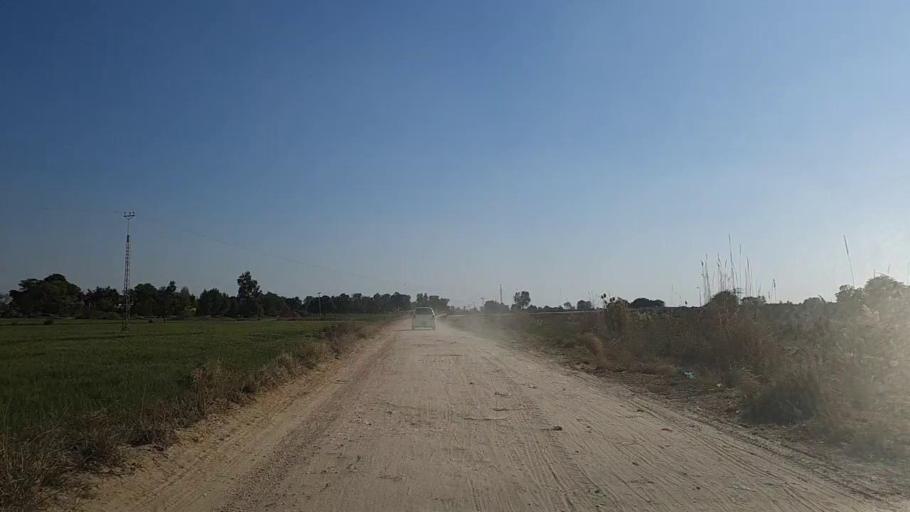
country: PK
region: Sindh
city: Nawabshah
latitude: 26.2334
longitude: 68.4262
